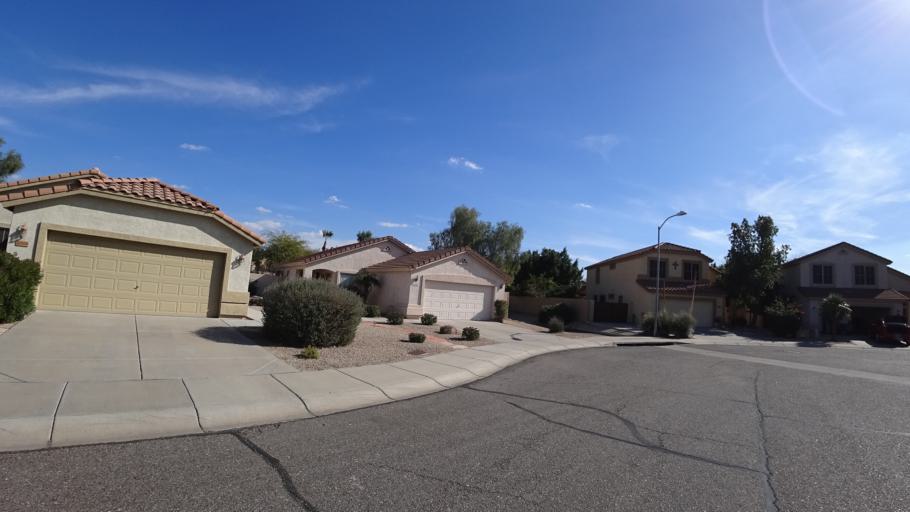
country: US
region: Arizona
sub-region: Maricopa County
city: Sun City
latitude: 33.6806
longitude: -112.2173
